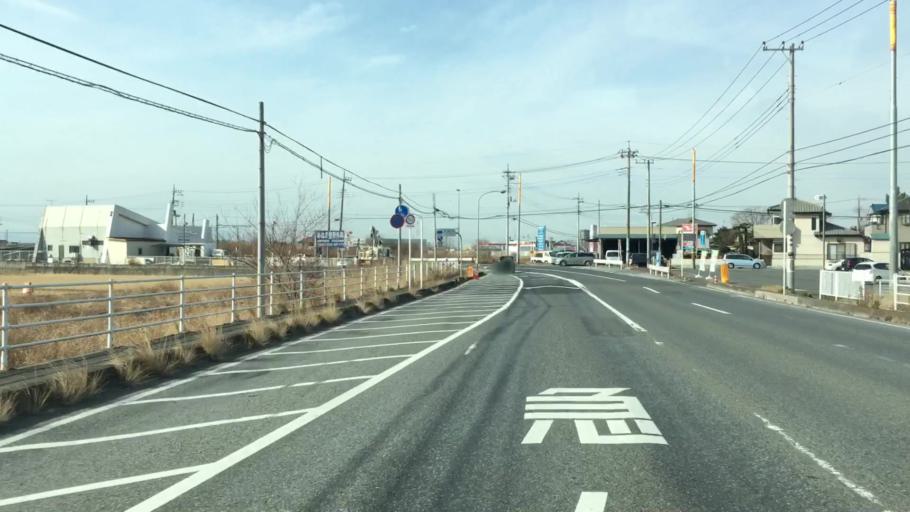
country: JP
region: Saitama
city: Menuma
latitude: 36.2449
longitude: 139.3849
